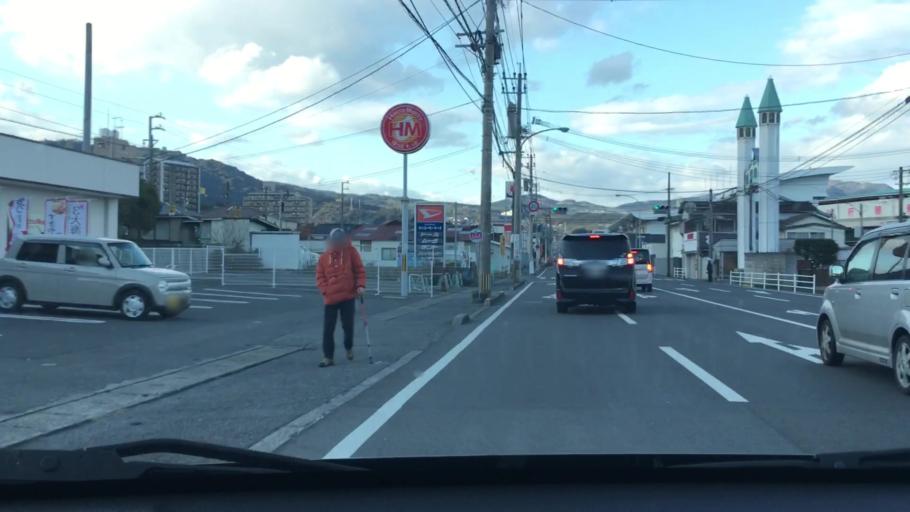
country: JP
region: Oita
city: Beppu
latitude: 33.3206
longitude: 131.4984
